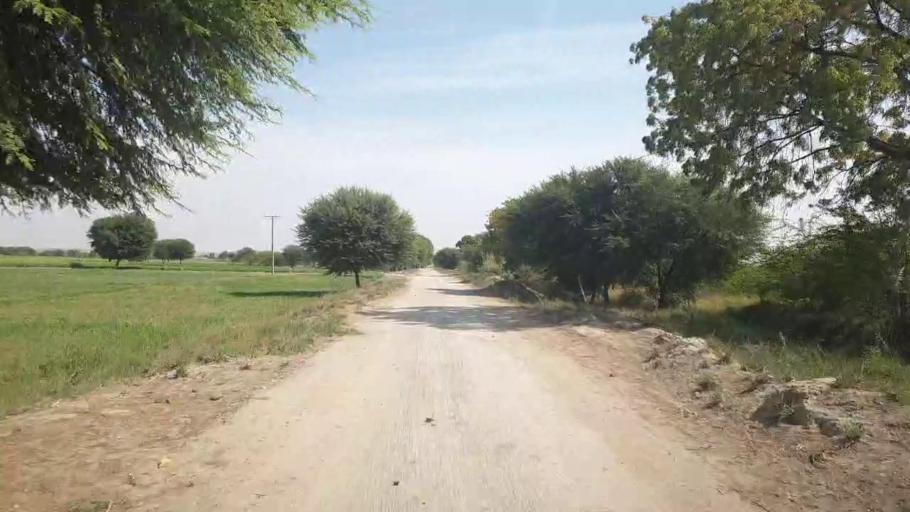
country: PK
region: Sindh
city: Kunri
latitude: 25.1910
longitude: 69.6832
